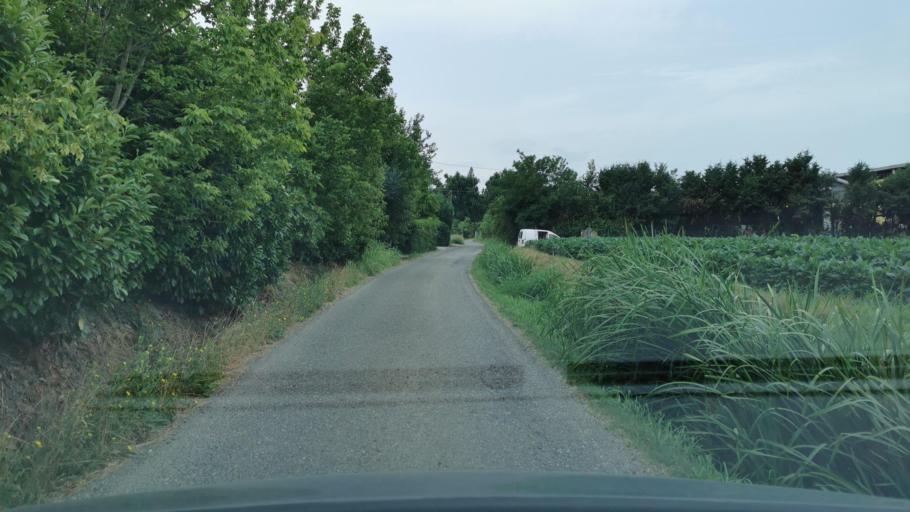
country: IT
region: Emilia-Romagna
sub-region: Provincia di Modena
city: Villanova
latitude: 44.6942
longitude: 10.8838
